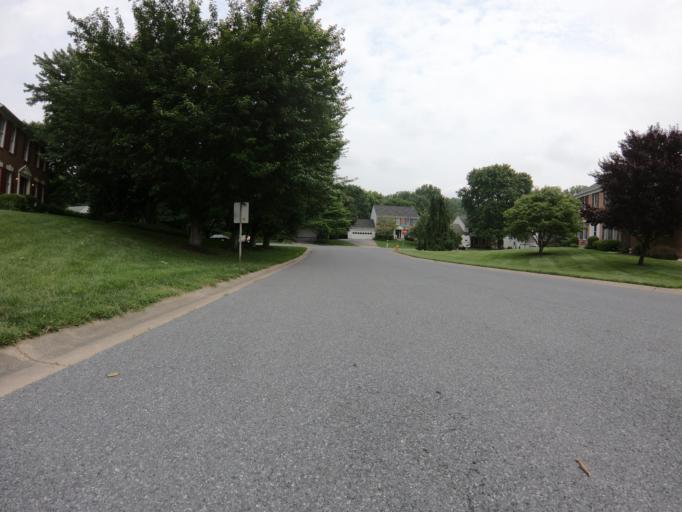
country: US
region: Maryland
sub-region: Howard County
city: Columbia
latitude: 39.2600
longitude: -76.8595
